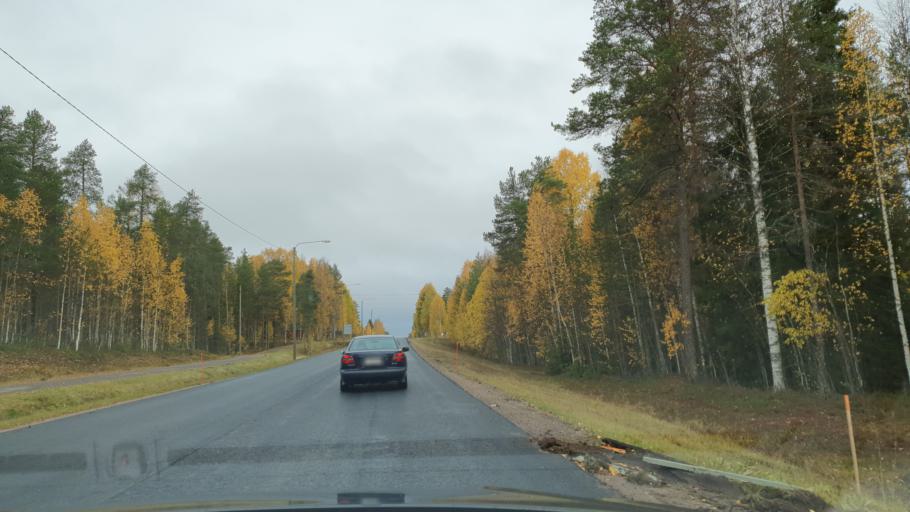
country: FI
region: Lapland
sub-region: Rovaniemi
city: Rovaniemi
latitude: 66.6505
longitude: 25.4540
